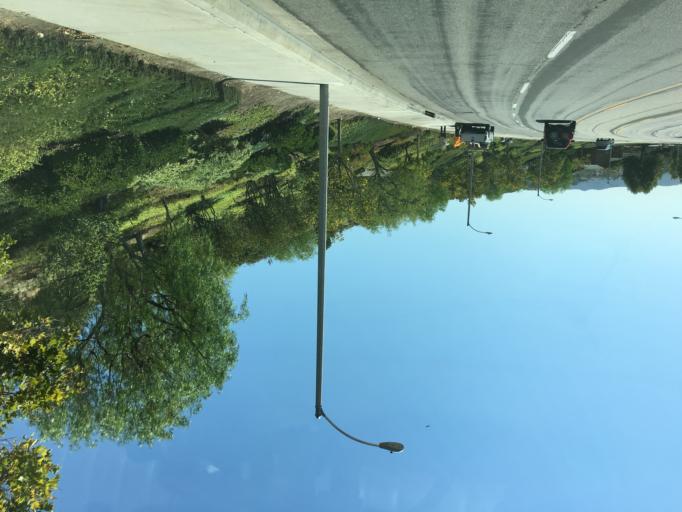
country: US
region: California
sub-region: Los Angeles County
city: Santa Clarita
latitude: 34.3889
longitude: -118.5832
